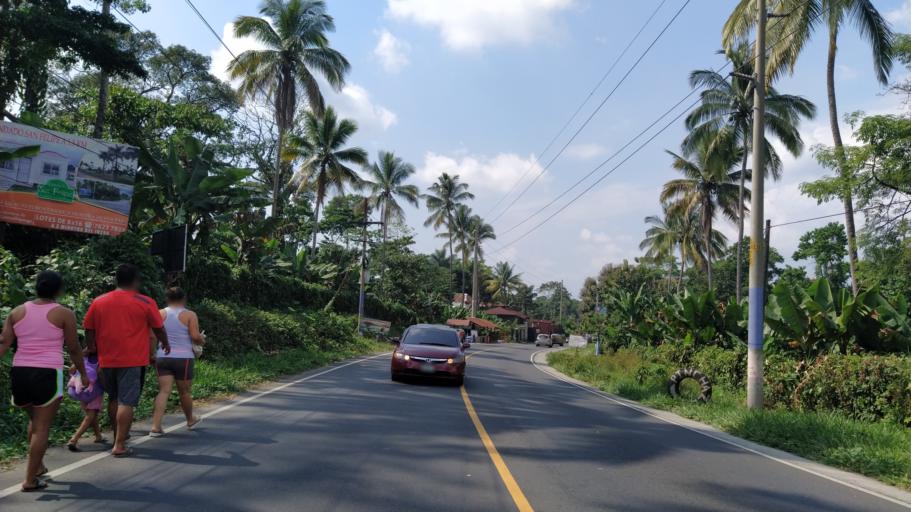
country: GT
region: Quetzaltenango
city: El Palmar
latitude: 14.6335
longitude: -91.5819
